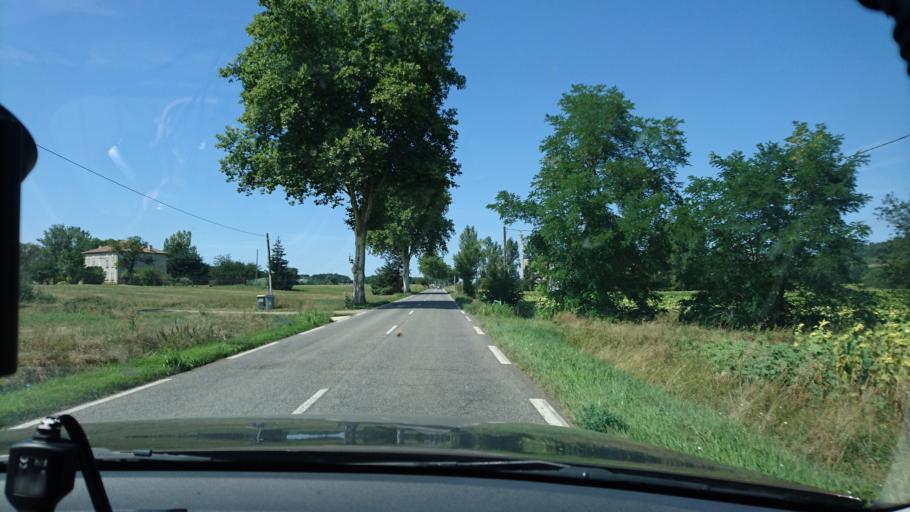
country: FR
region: Midi-Pyrenees
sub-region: Departement de l'Ariege
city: Lezat-sur-Leze
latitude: 43.2362
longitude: 1.3724
